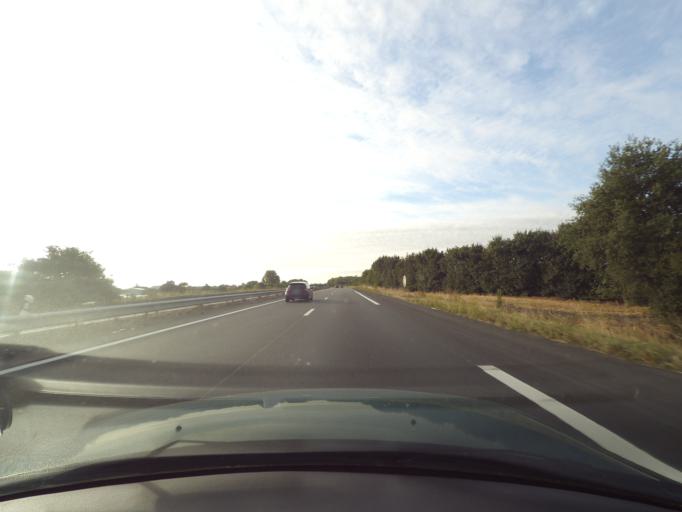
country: FR
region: Pays de la Loire
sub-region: Departement de Maine-et-Loire
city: Saint-Andre-de-la-Marche
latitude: 47.0962
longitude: -1.0127
